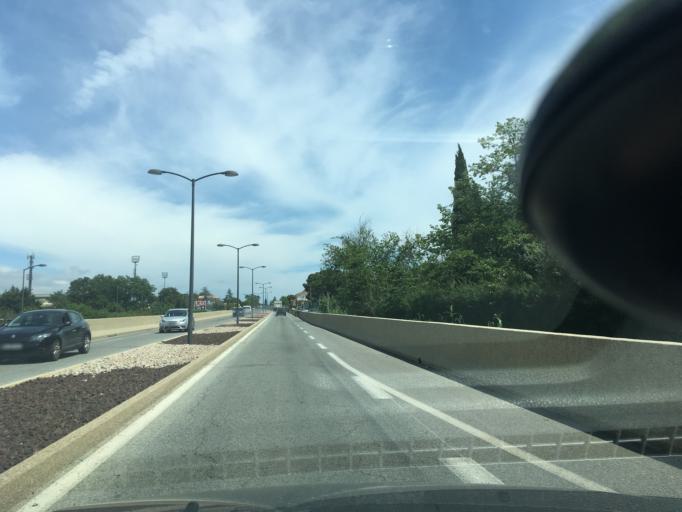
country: FR
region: Provence-Alpes-Cote d'Azur
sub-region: Departement du Var
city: Puget-sur-Argens
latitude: 43.4578
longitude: 6.6799
